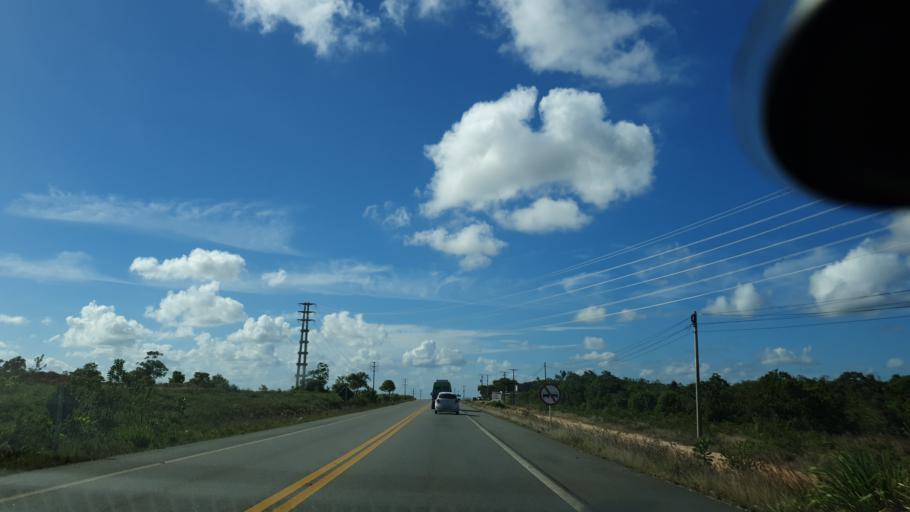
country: BR
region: Bahia
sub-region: Camacari
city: Camacari
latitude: -12.7015
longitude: -38.2155
